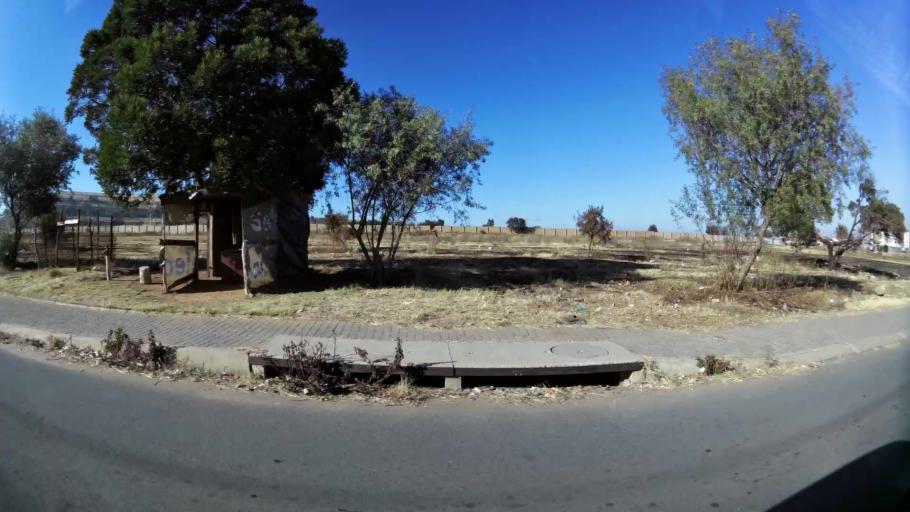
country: ZA
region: Gauteng
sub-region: City of Johannesburg Metropolitan Municipality
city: Roodepoort
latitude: -26.2170
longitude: 27.9435
